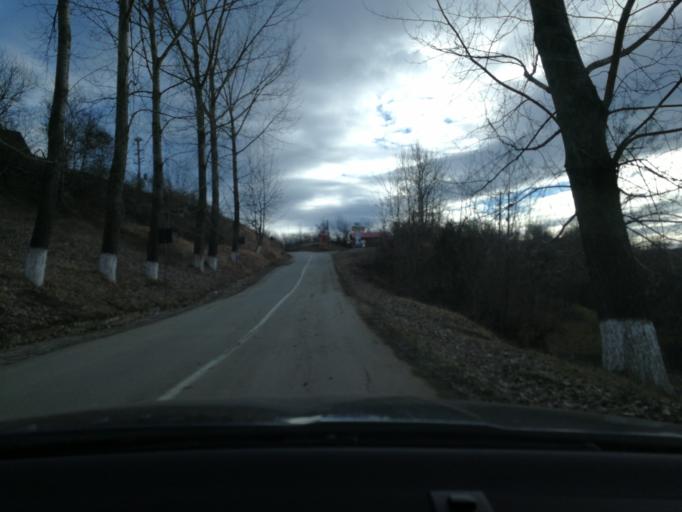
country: RO
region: Prahova
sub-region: Oras Breaza
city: Valea Tarsei
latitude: 45.1846
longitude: 25.6148
